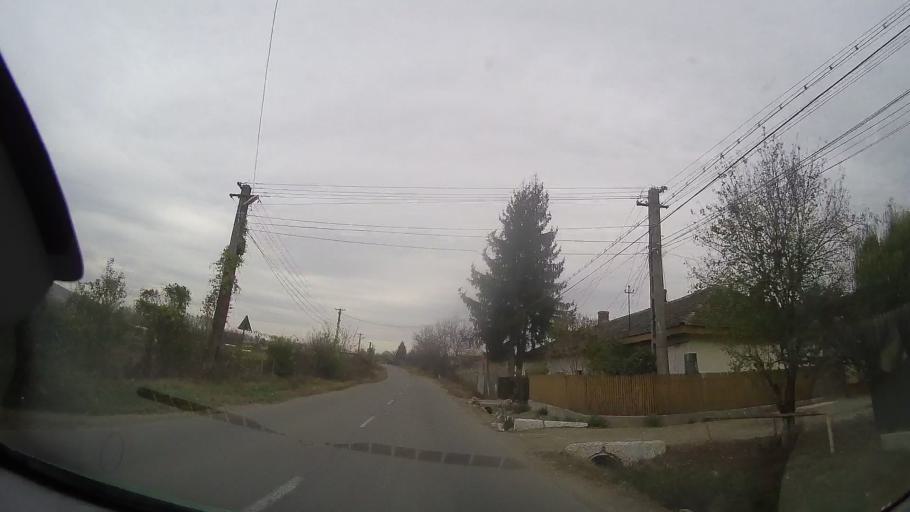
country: RO
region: Prahova
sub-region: Comuna Iordachianu
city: Iordacheanu
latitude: 45.0262
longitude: 26.2388
